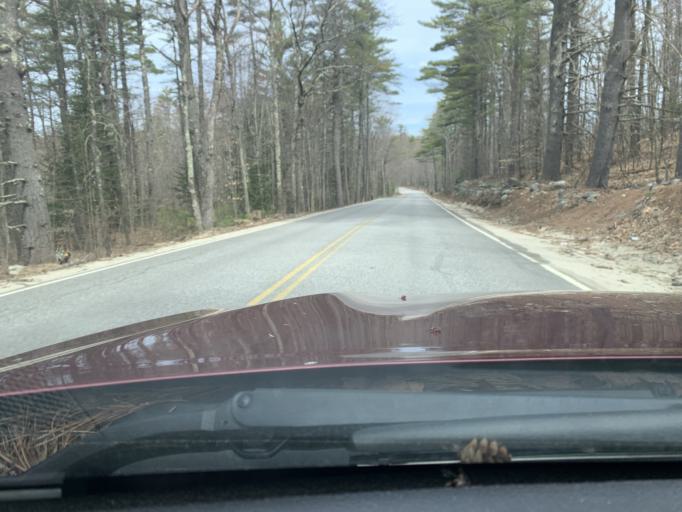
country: US
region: Maine
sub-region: Cumberland County
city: Raymond
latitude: 43.9471
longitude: -70.3862
